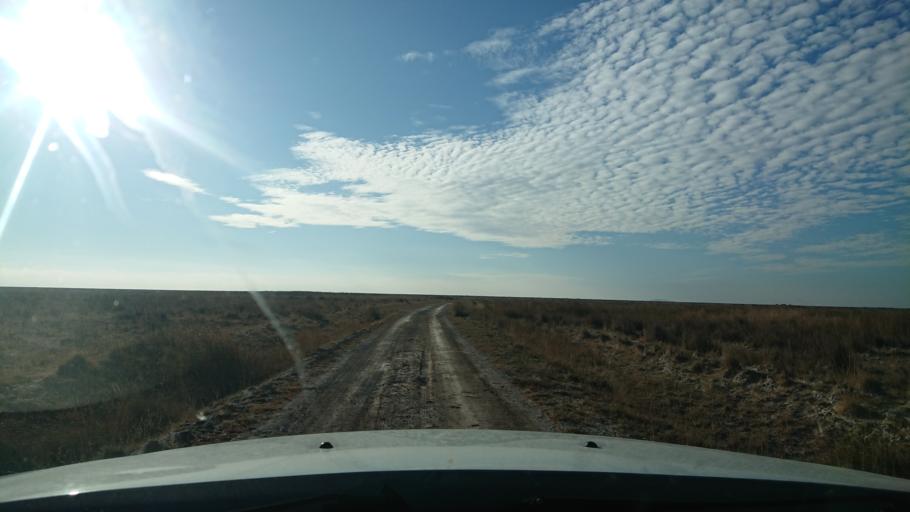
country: TR
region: Aksaray
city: Eskil
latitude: 38.5405
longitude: 33.3440
